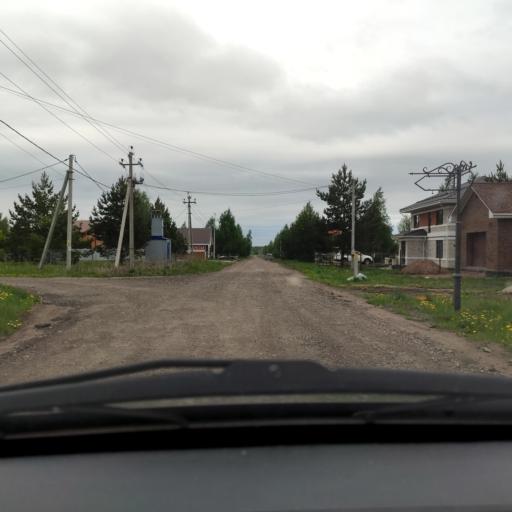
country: RU
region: Bashkortostan
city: Kabakovo
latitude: 54.6241
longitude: 56.1676
